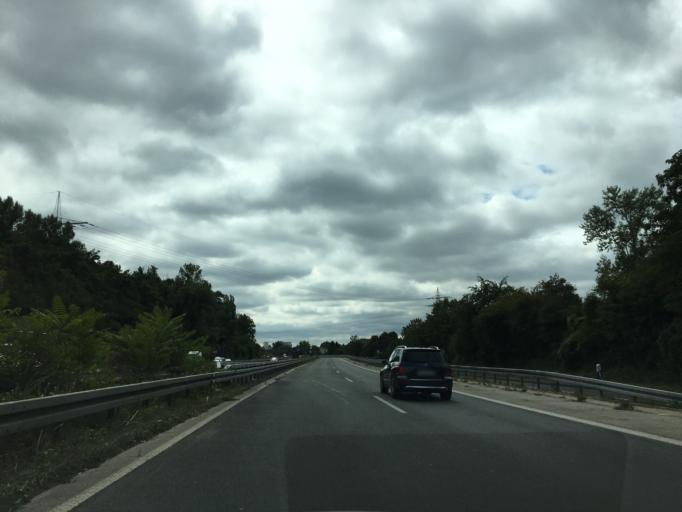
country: DE
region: Hesse
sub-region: Regierungsbezirk Darmstadt
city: Wiesbaden
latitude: 50.0481
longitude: 8.2562
